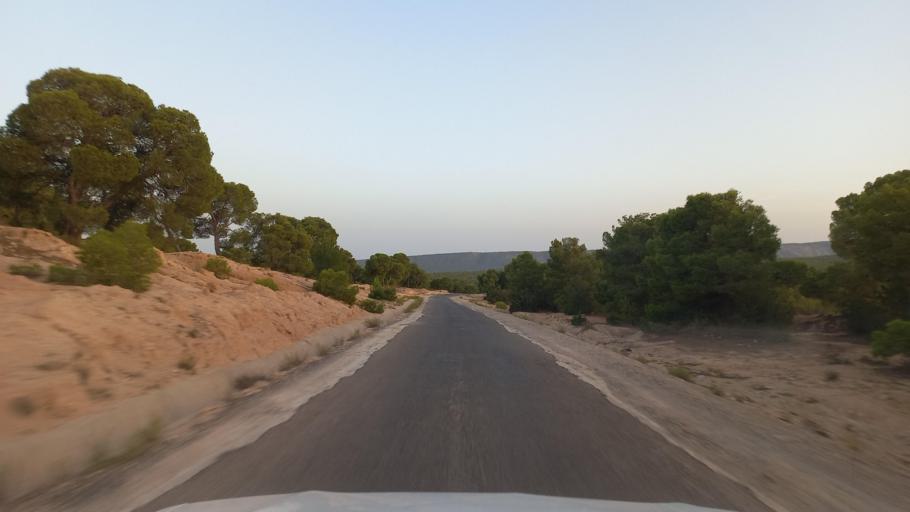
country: TN
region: Al Qasrayn
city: Sbiba
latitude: 35.4190
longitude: 8.9247
